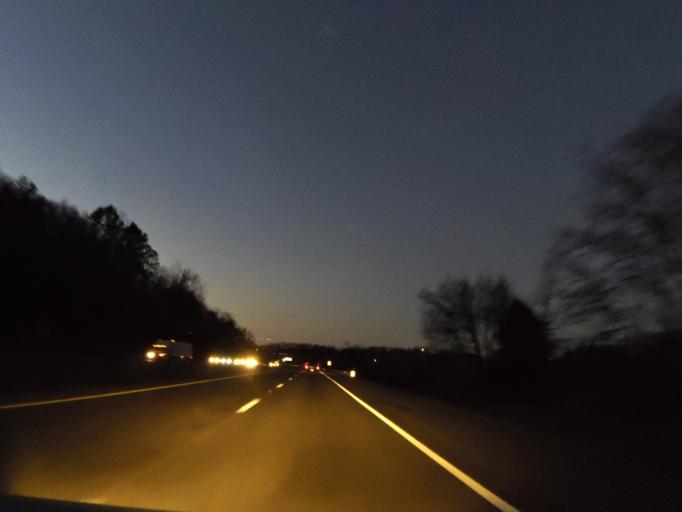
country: US
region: Tennessee
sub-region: Cocke County
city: Newport
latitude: 35.9759
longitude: -83.2715
